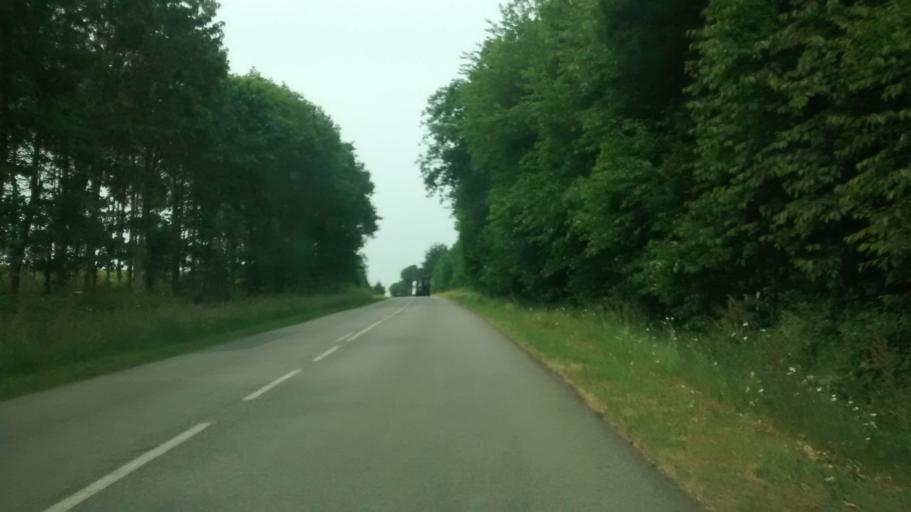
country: FR
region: Brittany
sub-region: Departement du Morbihan
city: Ruffiac
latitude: 47.8497
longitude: -2.2626
